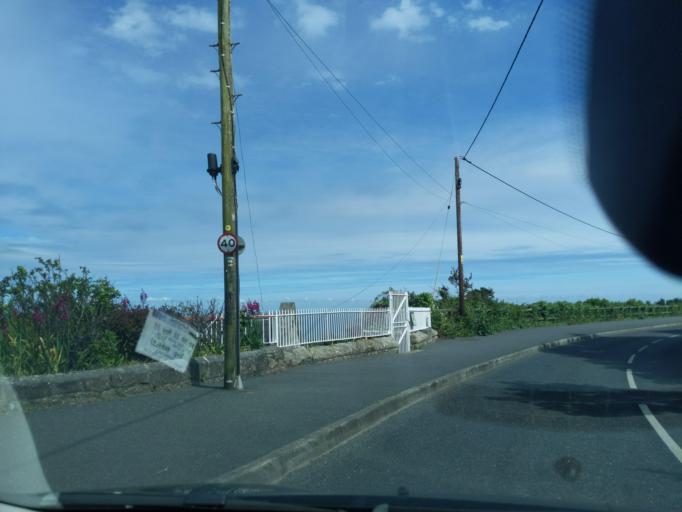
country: GB
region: England
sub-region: Cornwall
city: Penzance
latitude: 50.0892
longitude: -5.5344
